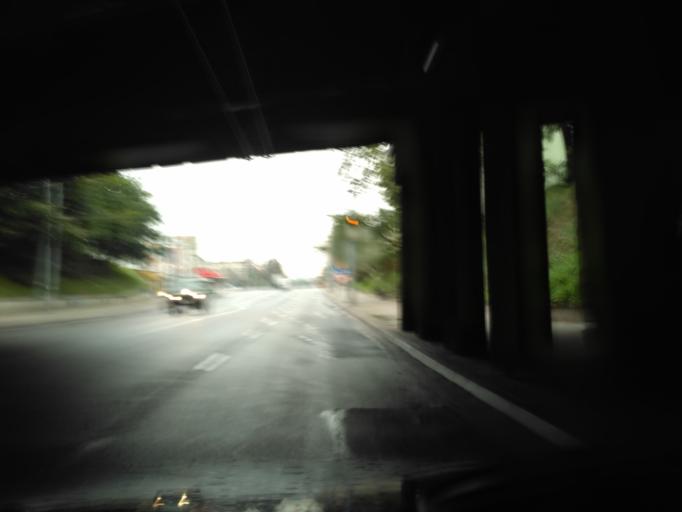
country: PL
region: Lublin Voivodeship
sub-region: Powiat lubelski
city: Lublin
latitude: 51.2358
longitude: 22.5788
